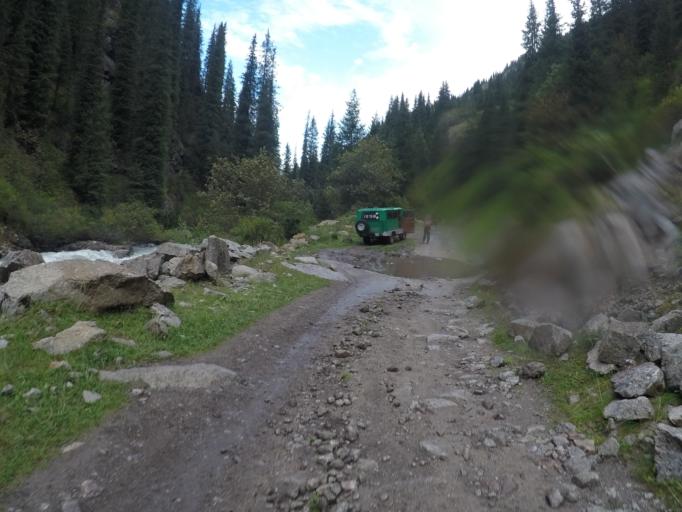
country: KG
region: Ysyk-Koel
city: Teploklyuchenka
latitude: 42.4166
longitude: 78.5722
